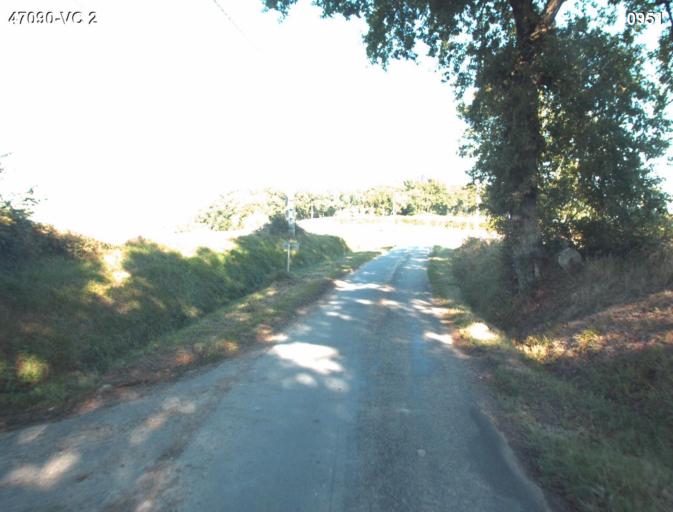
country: FR
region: Aquitaine
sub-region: Departement du Lot-et-Garonne
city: Vianne
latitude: 44.1828
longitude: 0.3662
